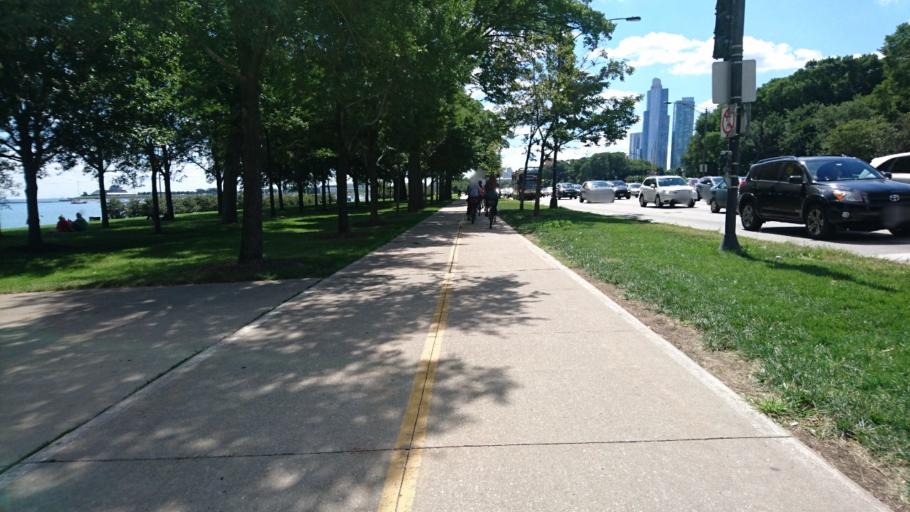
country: US
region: Illinois
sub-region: Cook County
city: Chicago
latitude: 41.8783
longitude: -87.6170
